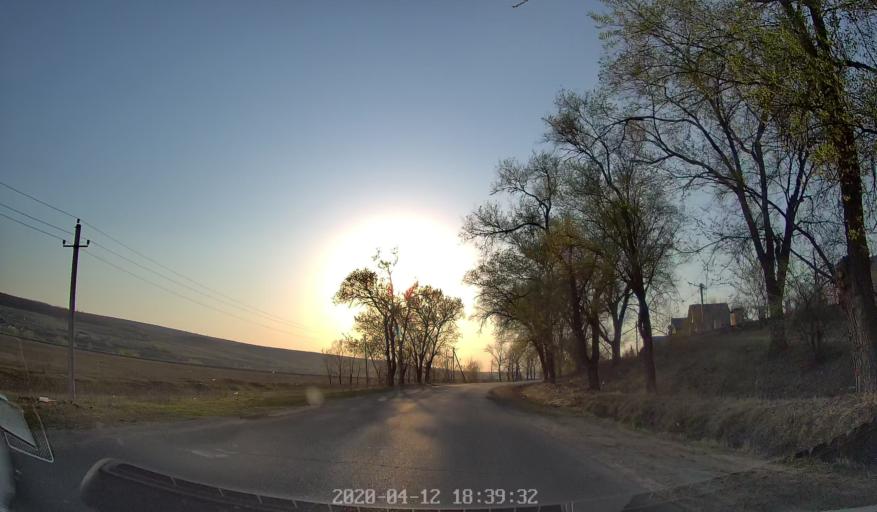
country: MD
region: Chisinau
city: Ciorescu
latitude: 47.1285
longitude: 28.9835
